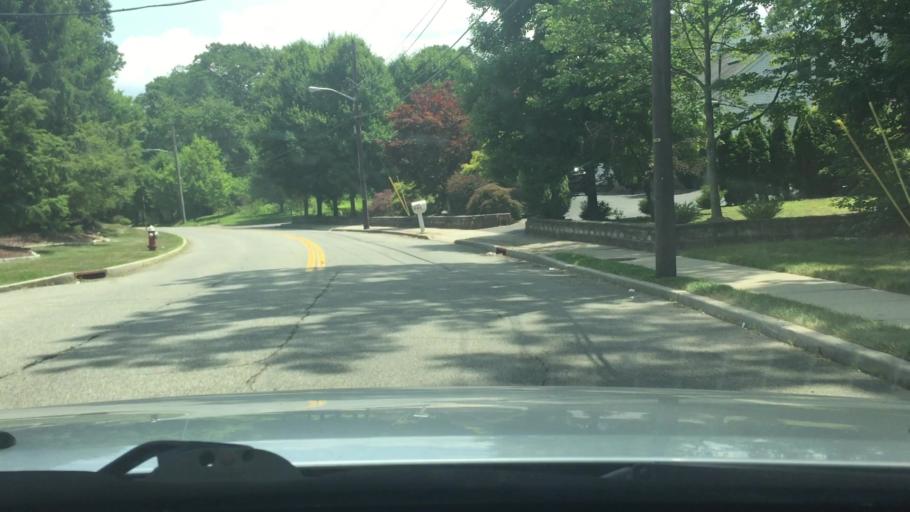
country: US
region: New Jersey
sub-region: Middlesex County
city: East Brunswick
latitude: 40.4143
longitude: -74.4105
